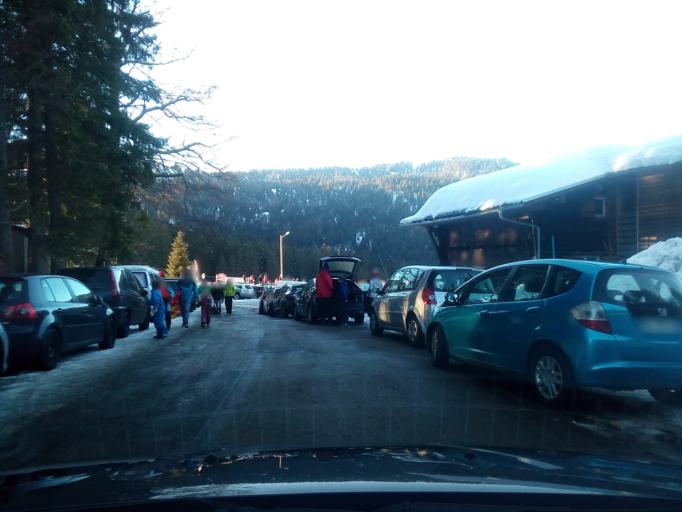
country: FR
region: Rhone-Alpes
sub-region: Departement de l'Isere
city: Le Sappey-en-Chartreuse
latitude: 45.2941
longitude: 5.7656
